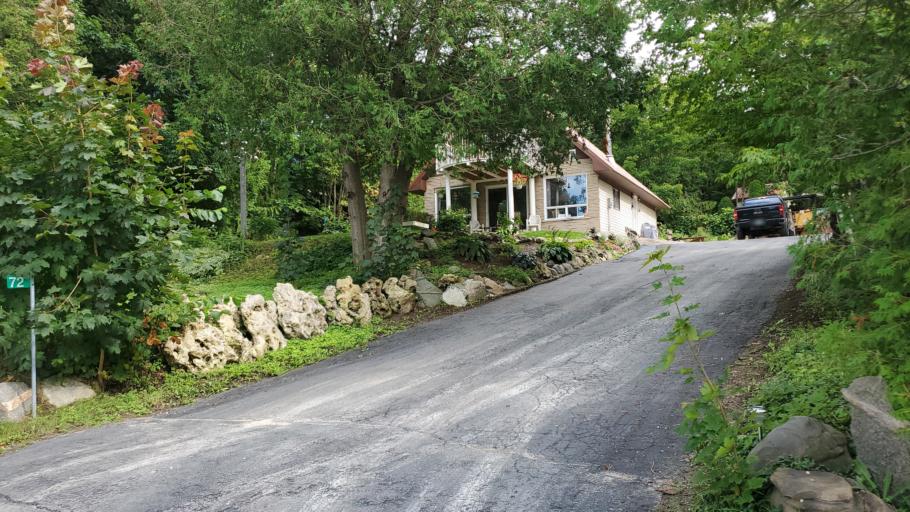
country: CA
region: Ontario
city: Owen Sound
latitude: 44.9014
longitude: -81.1486
